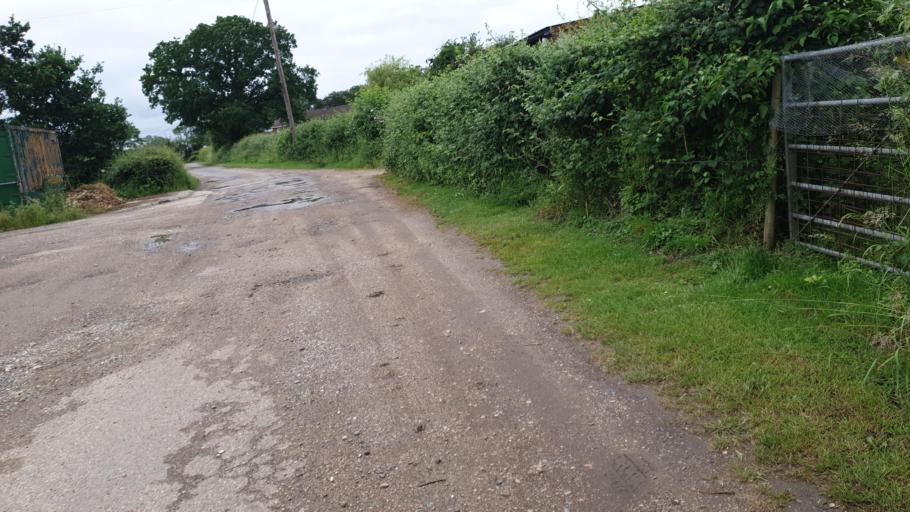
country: GB
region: England
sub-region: Essex
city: Great Bentley
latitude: 51.8788
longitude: 1.0588
